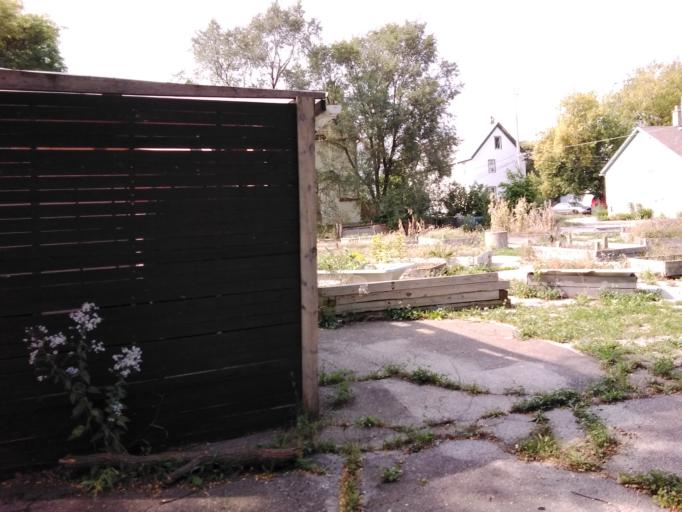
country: US
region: Wisconsin
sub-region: Milwaukee County
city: Milwaukee
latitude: 43.0474
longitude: -87.9404
